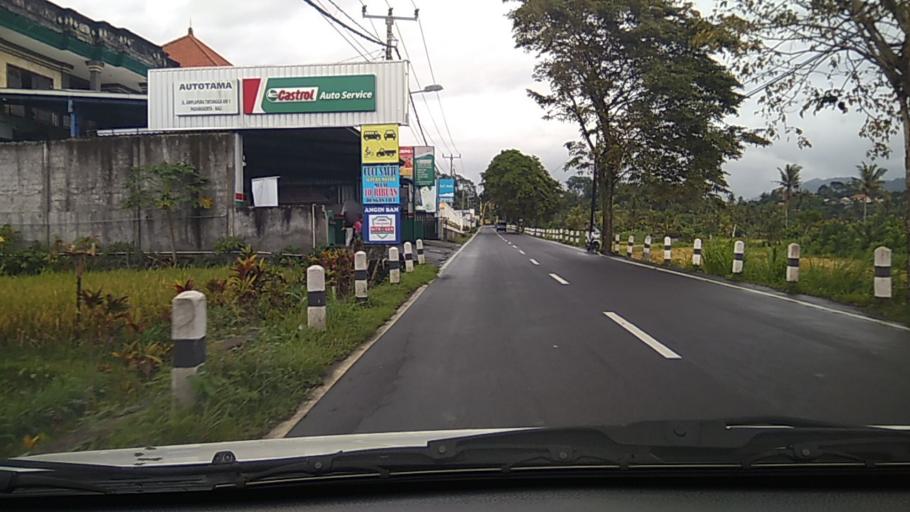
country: ID
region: Bali
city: Banjar Budakeling
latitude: -8.4287
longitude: 115.5921
